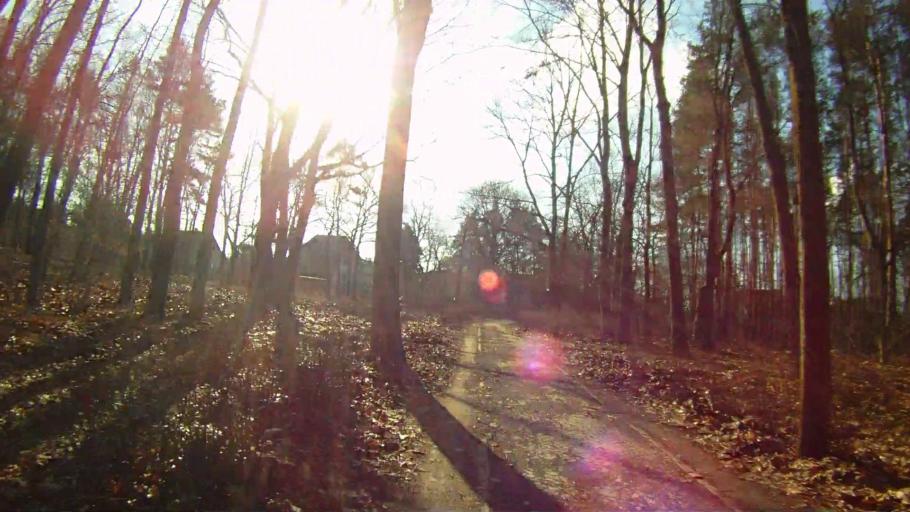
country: DE
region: Berlin
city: Rahnsdorf
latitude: 52.4456
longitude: 13.6916
